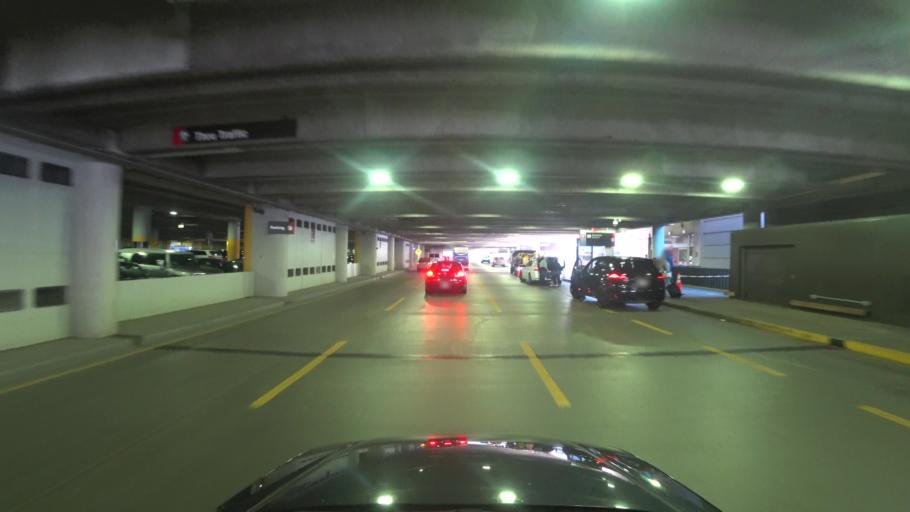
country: US
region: Massachusetts
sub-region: Suffolk County
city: Chelsea
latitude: 42.3628
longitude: -71.0188
